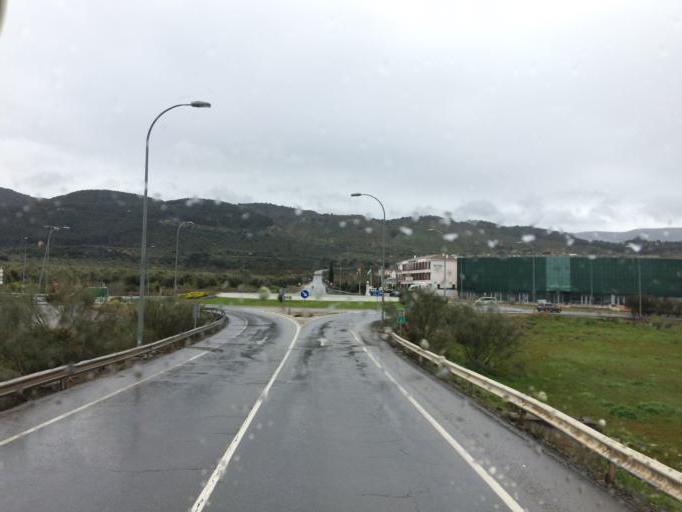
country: ES
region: Andalusia
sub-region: Provincia de Malaga
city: Antequera
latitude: 37.0350
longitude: -4.5290
